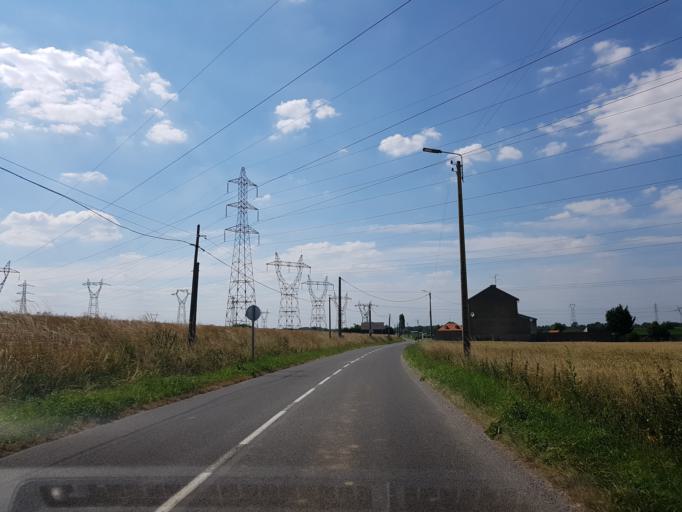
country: FR
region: Nord-Pas-de-Calais
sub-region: Departement du Nord
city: Roeulx
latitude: 50.3154
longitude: 3.3291
